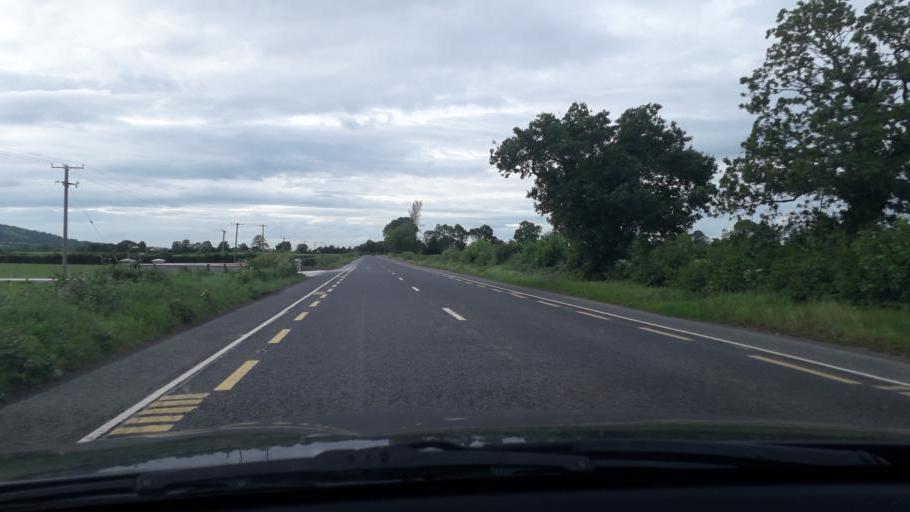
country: IE
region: Leinster
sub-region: County Carlow
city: Carlow
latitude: 52.7996
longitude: -6.9502
